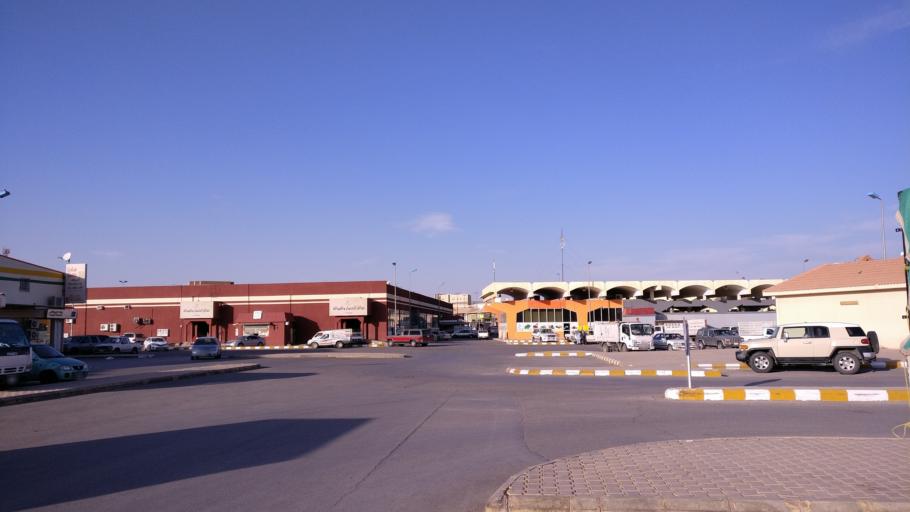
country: SA
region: Al-Qassim
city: Unaizah
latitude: 26.0876
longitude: 43.9668
